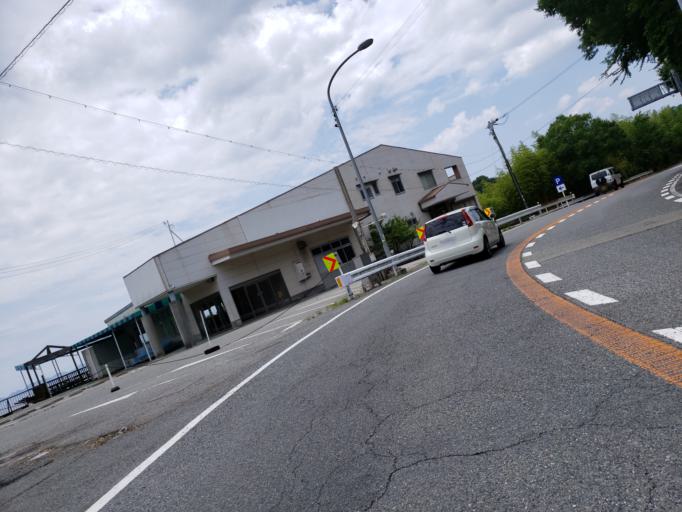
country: JP
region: Hyogo
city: Aioi
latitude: 34.7689
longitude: 134.5121
